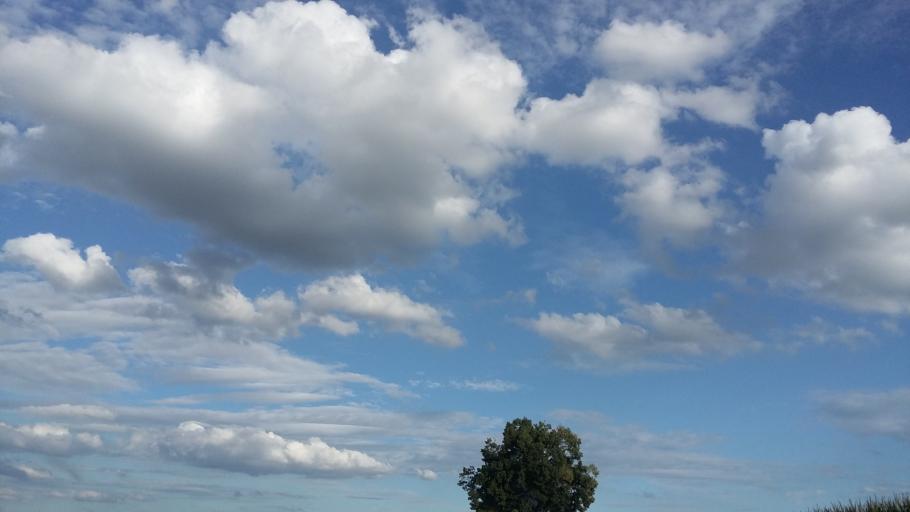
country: DE
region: Bavaria
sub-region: Swabia
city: Merching
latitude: 48.2375
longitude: 11.0037
